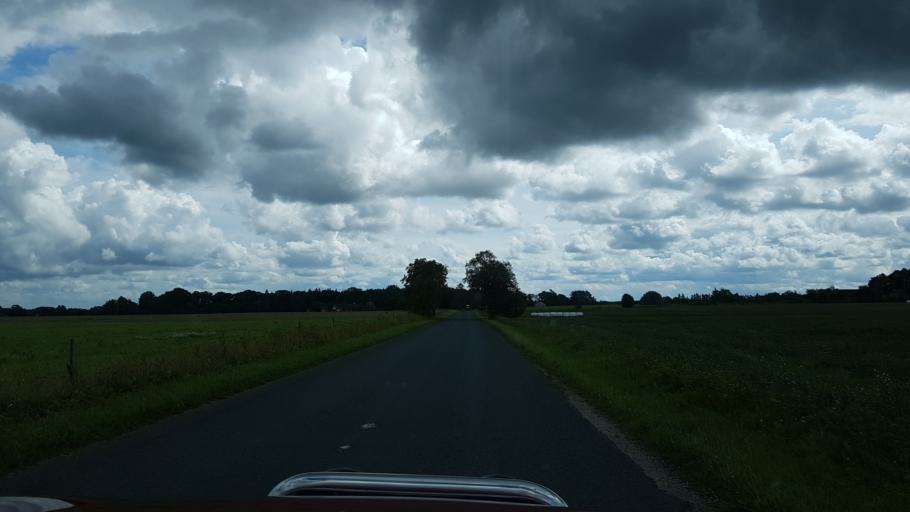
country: EE
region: Laeaene
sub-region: Lihula vald
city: Lihula
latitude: 58.7104
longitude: 24.0129
